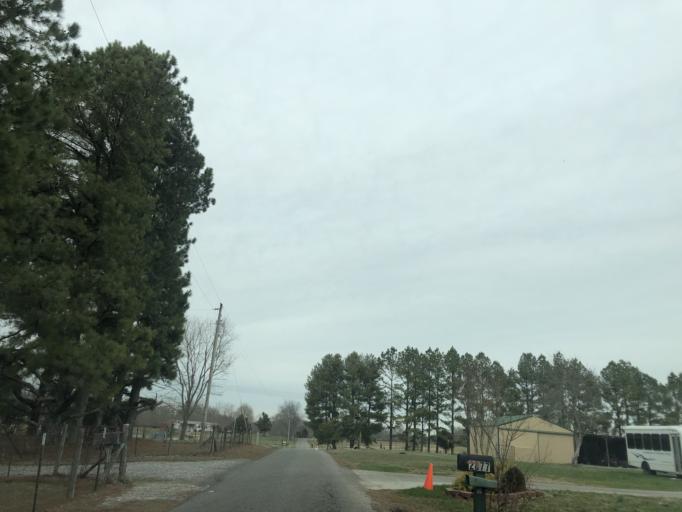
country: US
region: Tennessee
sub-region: Robertson County
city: Greenbrier
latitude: 36.4561
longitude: -86.7851
